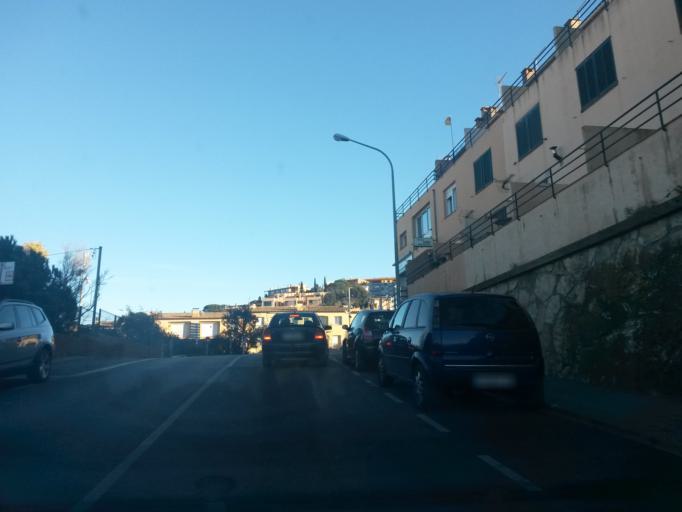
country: ES
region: Catalonia
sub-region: Provincia de Girona
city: Begur
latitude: 41.9528
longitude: 3.2057
